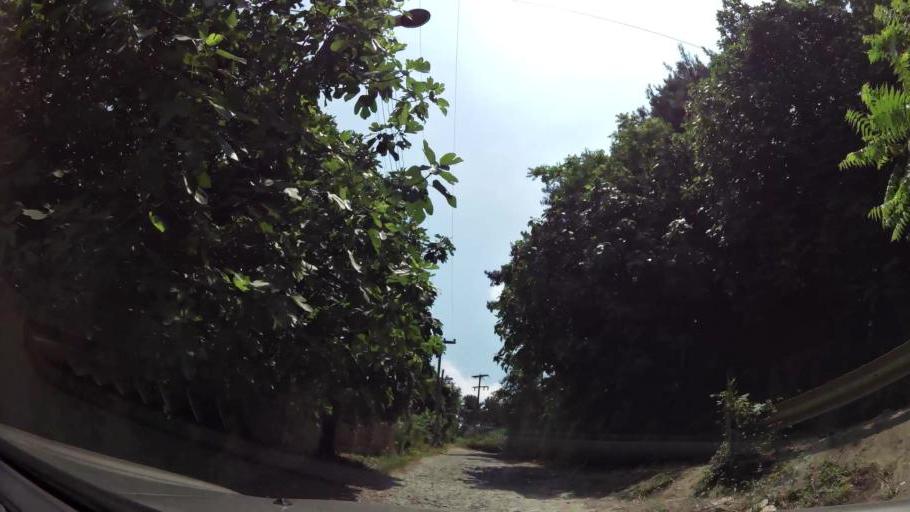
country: GR
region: Central Macedonia
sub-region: Nomos Imathias
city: Veroia
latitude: 40.5180
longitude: 22.1958
